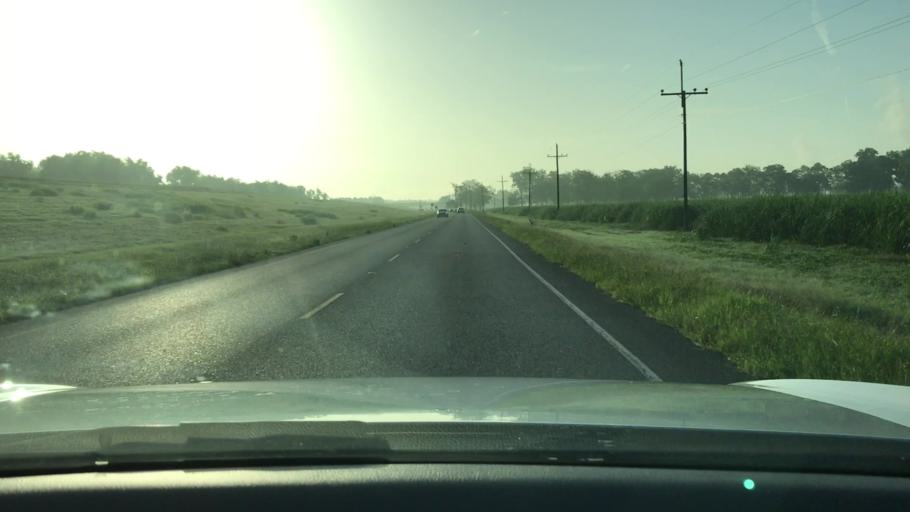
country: US
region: Louisiana
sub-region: Iberville Parish
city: Plaquemine
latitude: 30.2727
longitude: -91.1926
